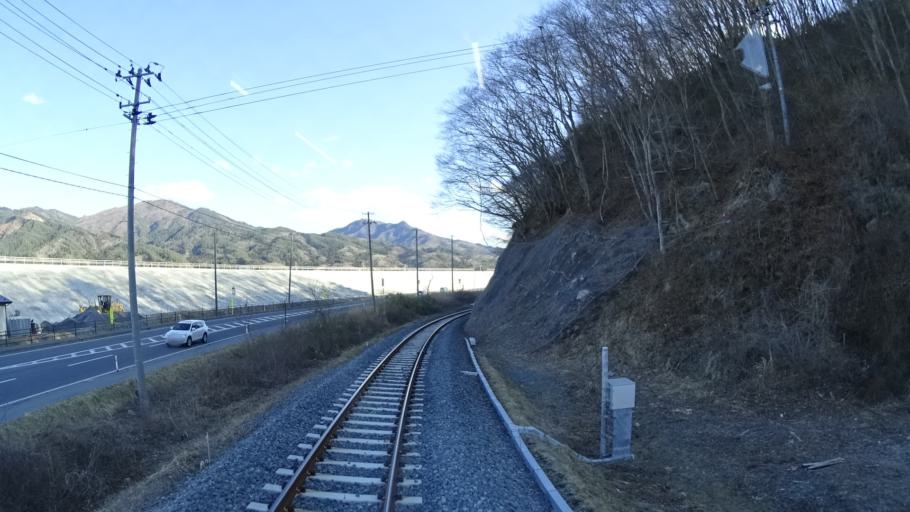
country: JP
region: Iwate
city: Miyako
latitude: 39.5898
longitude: 141.9462
